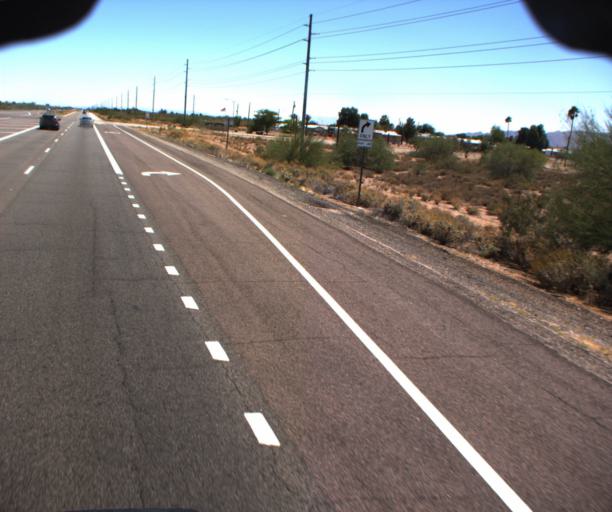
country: US
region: Arizona
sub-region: Maricopa County
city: Sun City West
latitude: 33.7896
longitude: -112.5439
